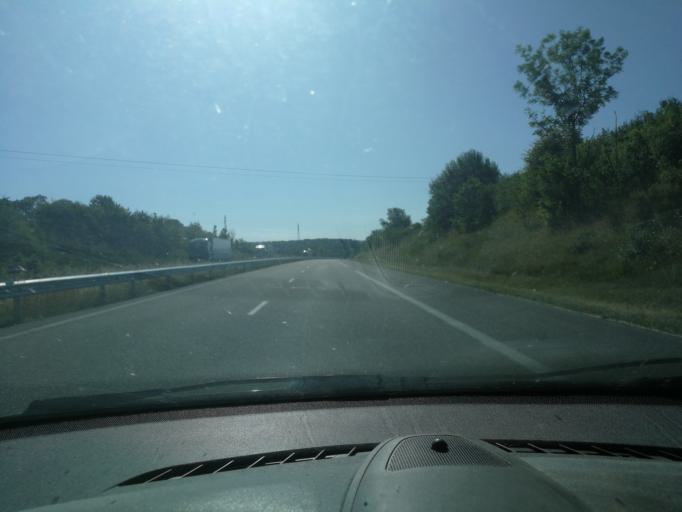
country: FR
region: Alsace
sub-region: Departement du Bas-Rhin
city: Drulingen
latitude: 48.8089
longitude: 7.1682
